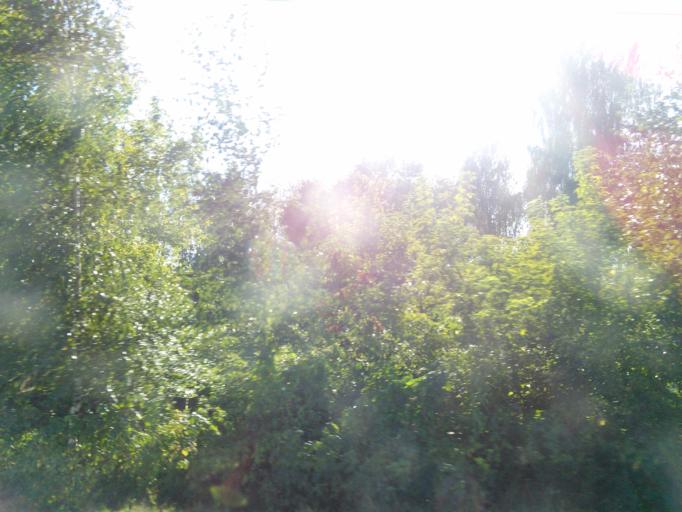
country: RU
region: Jaroslavl
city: Rybinsk
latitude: 58.0566
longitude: 38.8564
